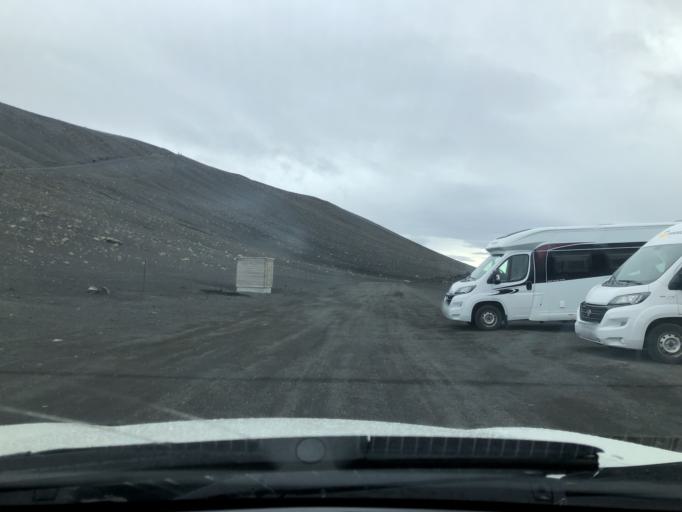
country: IS
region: Northeast
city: Laugar
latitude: 65.6129
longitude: -16.8758
